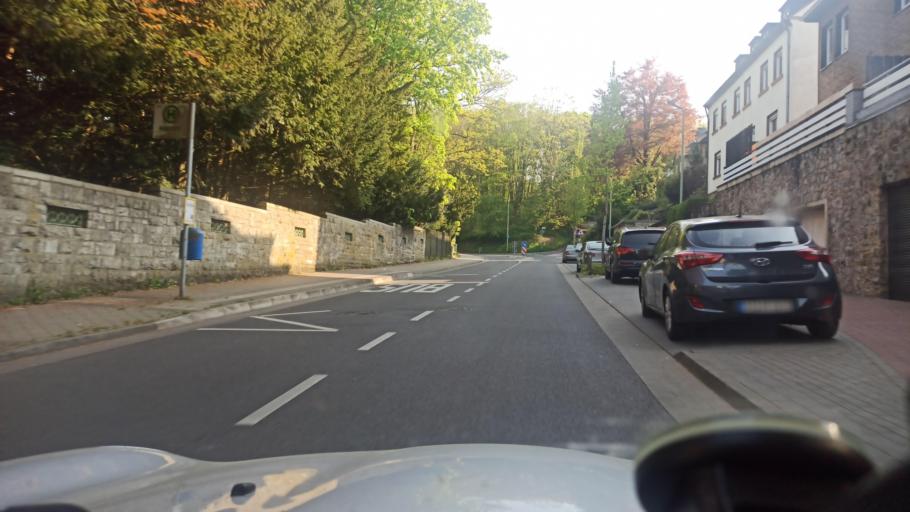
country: DE
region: North Rhine-Westphalia
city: Stolberg
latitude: 50.7622
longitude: 6.2281
